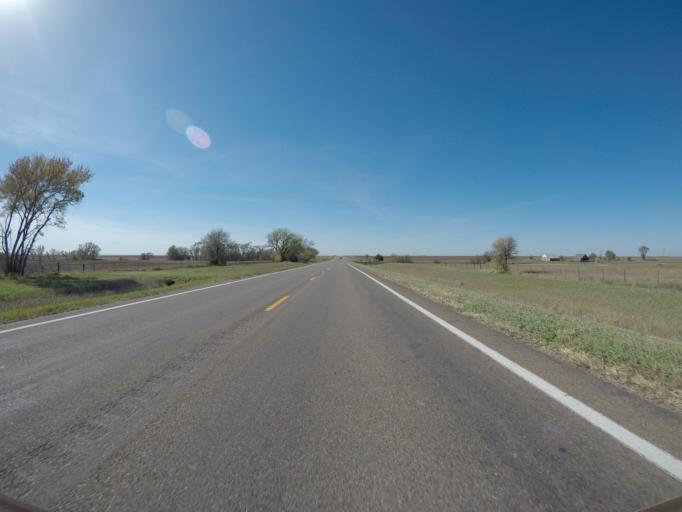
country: US
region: Kansas
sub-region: Smith County
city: Smith Center
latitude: 39.7710
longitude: -98.9419
